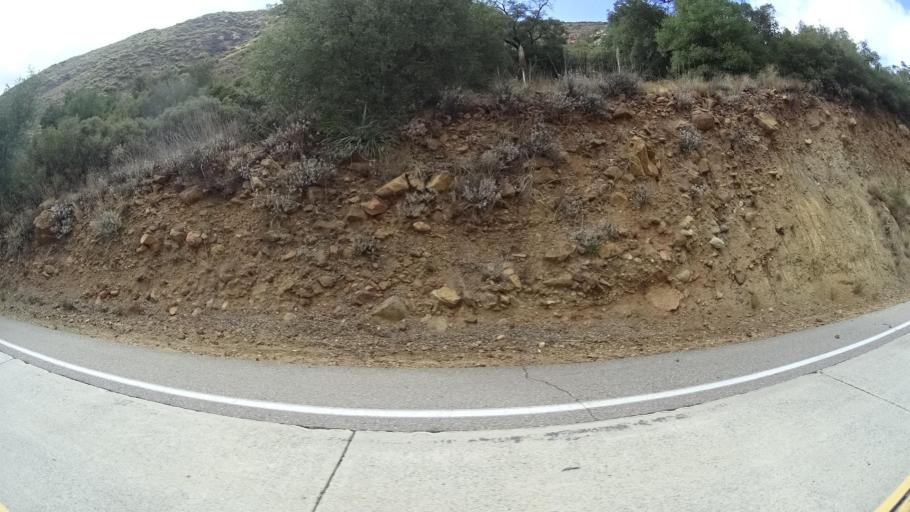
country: US
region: California
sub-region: San Diego County
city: Pine Valley
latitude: 32.7889
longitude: -116.4973
